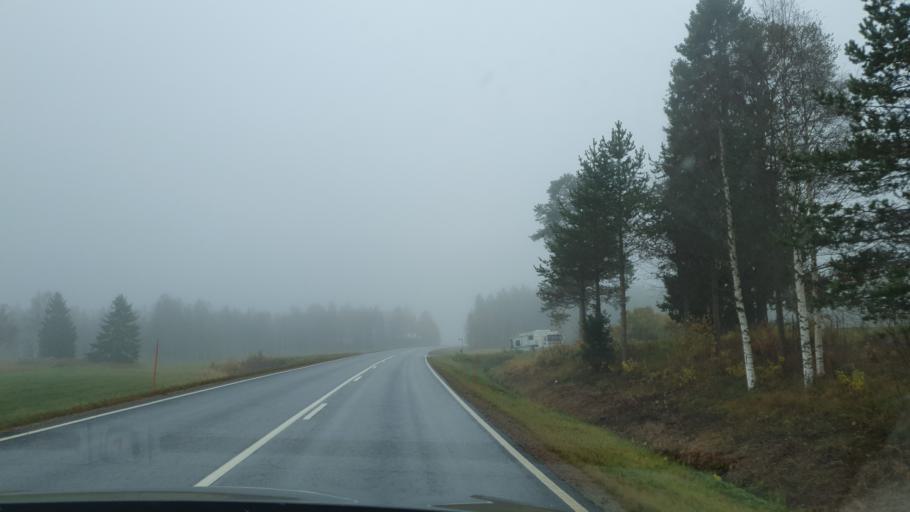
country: FI
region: Lapland
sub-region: Rovaniemi
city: Rovaniemi
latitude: 66.8062
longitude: 25.4120
